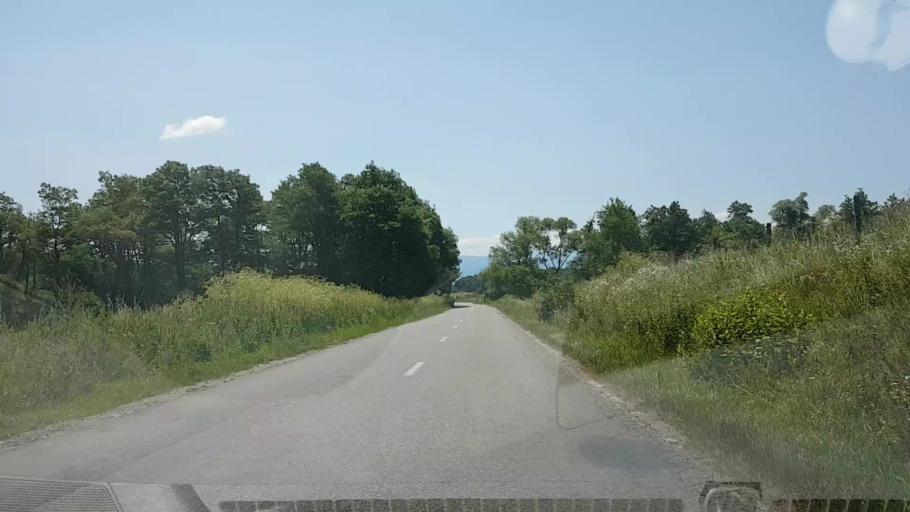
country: RO
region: Brasov
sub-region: Comuna Cincu
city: Cincu
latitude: 45.8801
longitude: 24.8145
